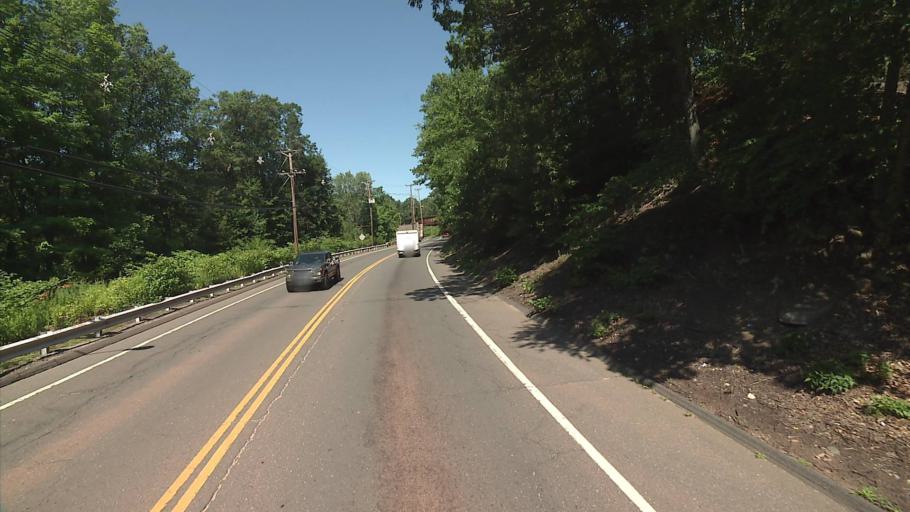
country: US
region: Connecticut
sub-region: Litchfield County
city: Terryville
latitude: 41.6701
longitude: -72.9832
